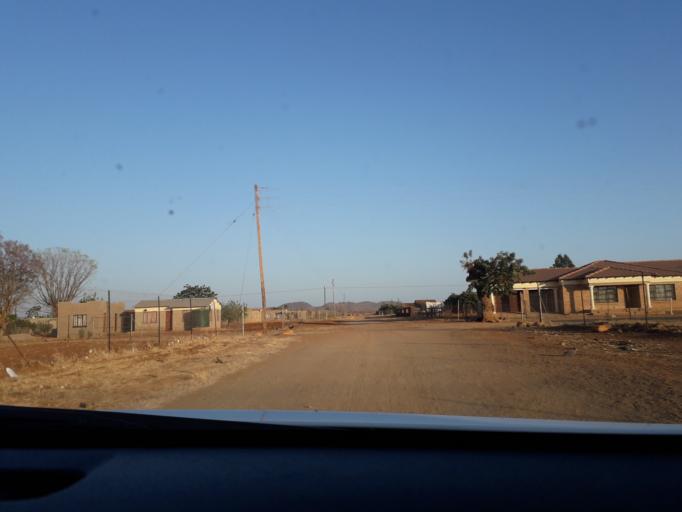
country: ZA
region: Limpopo
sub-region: Waterberg District Municipality
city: Mokopane
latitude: -23.9161
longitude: 28.8707
